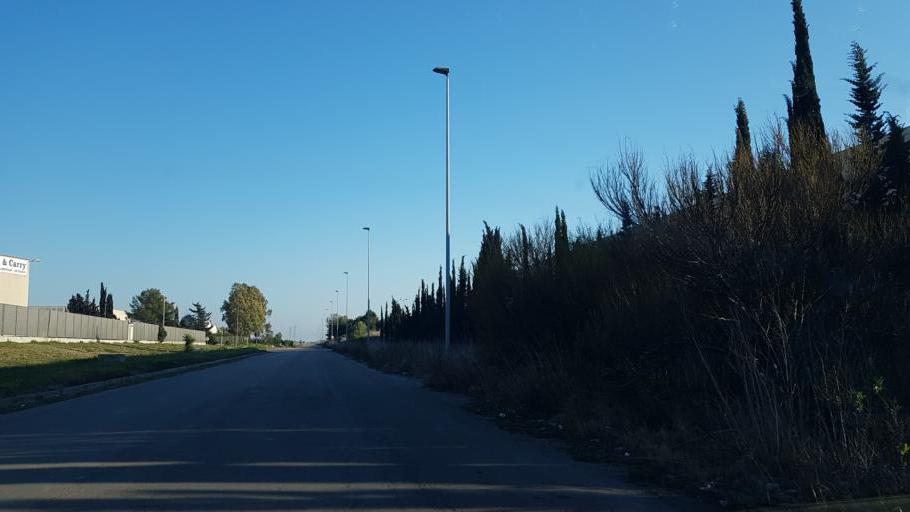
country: IT
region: Apulia
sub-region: Provincia di Brindisi
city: La Rosa
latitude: 40.6266
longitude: 17.9674
